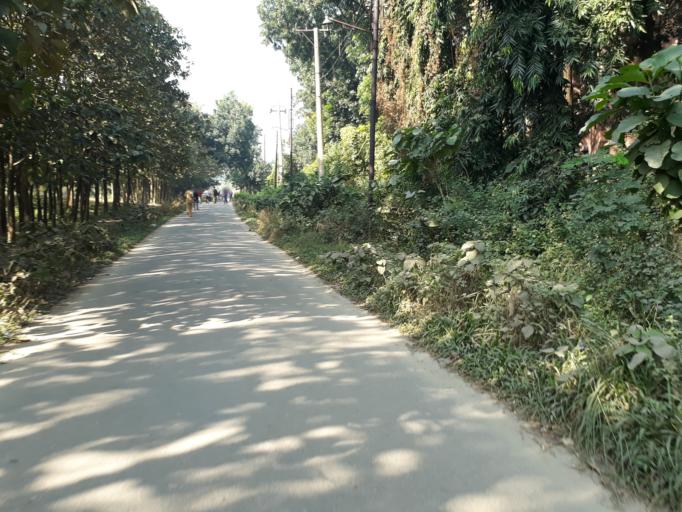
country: BD
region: Dhaka
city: Tungi
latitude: 23.8798
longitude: 90.2641
